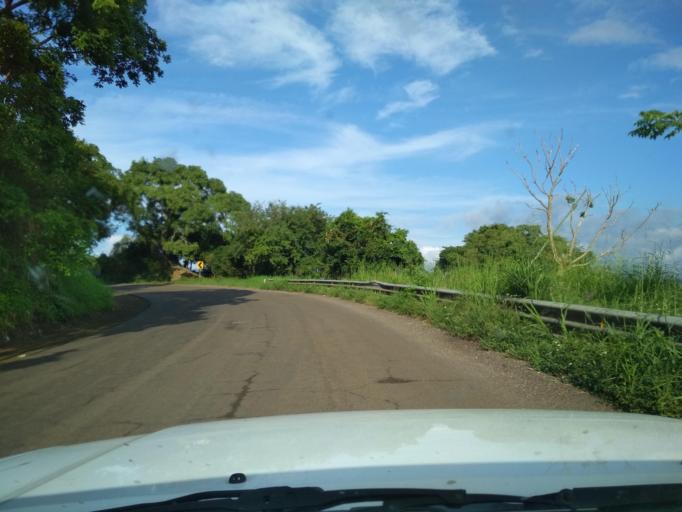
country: MX
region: Veracruz
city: Catemaco
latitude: 18.3861
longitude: -95.1231
